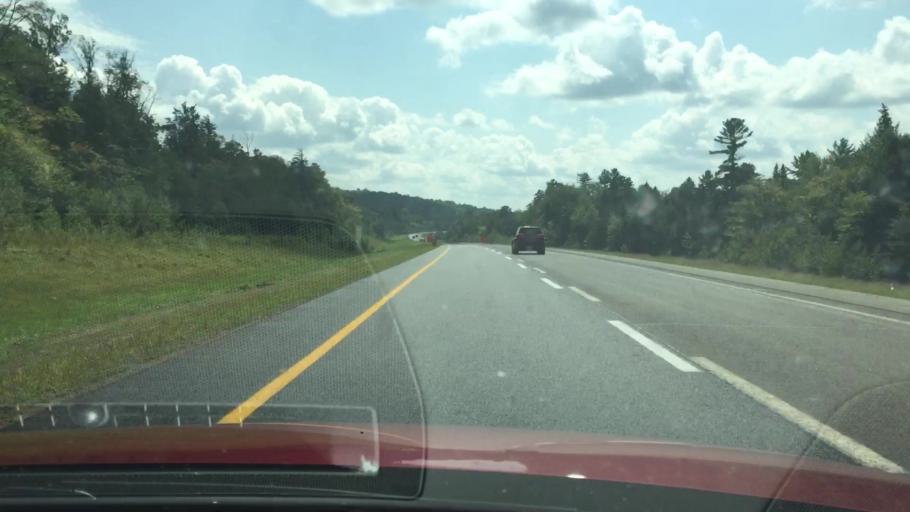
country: US
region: Maine
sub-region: Penobscot County
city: Medway
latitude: 45.7201
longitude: -68.4753
